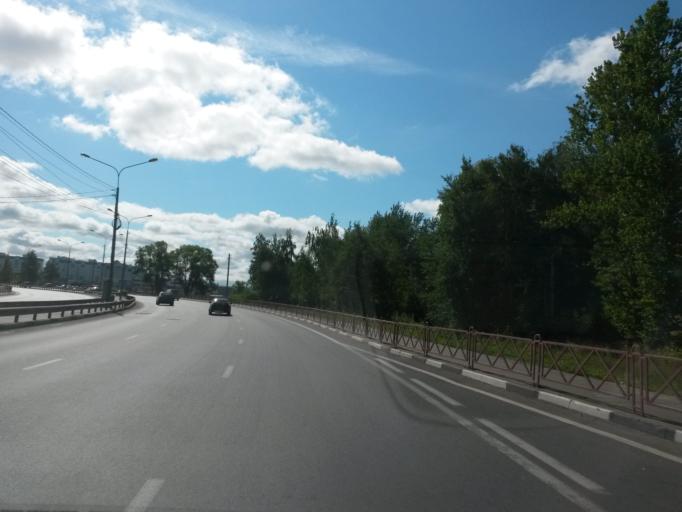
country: RU
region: Jaroslavl
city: Yaroslavl
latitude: 57.5945
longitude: 39.8935
